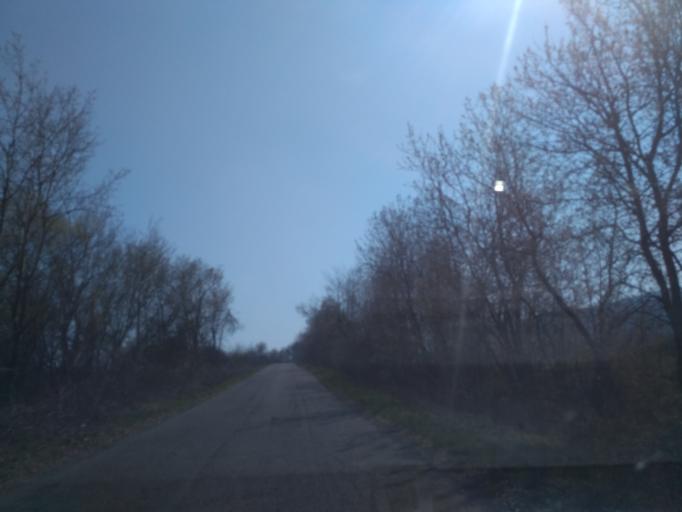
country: SK
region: Presovsky
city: Vranov nad Topl'ou
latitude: 48.8186
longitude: 21.6378
